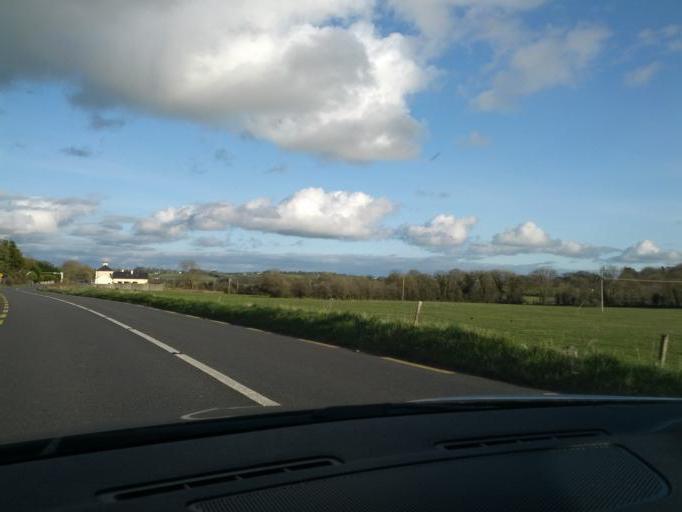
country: IE
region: Connaught
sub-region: Roscommon
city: Roscommon
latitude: 53.6653
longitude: -8.3012
